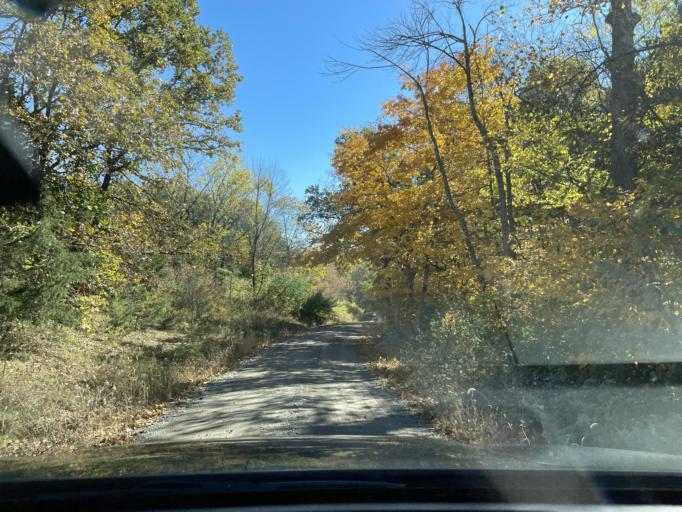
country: US
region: Missouri
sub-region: Andrew County
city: Savannah
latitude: 39.9377
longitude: -94.8668
